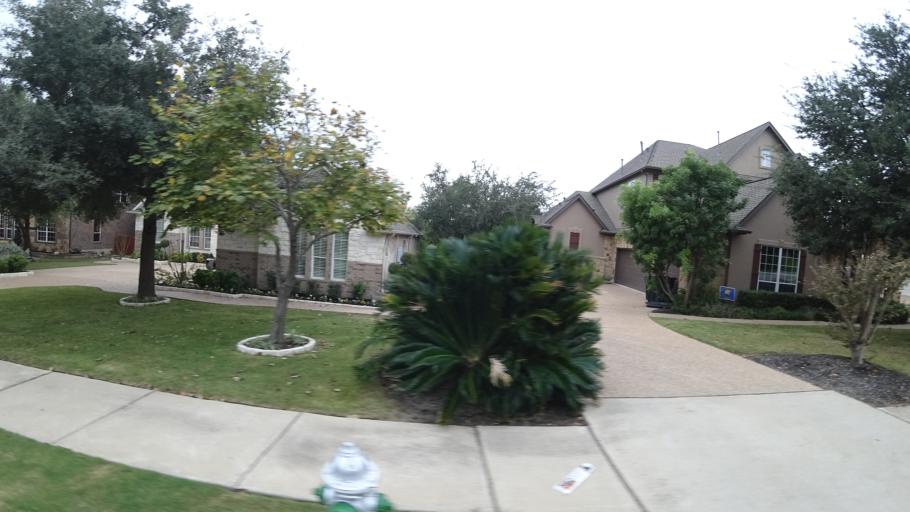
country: US
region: Texas
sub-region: Travis County
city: Bee Cave
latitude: 30.3571
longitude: -97.9027
